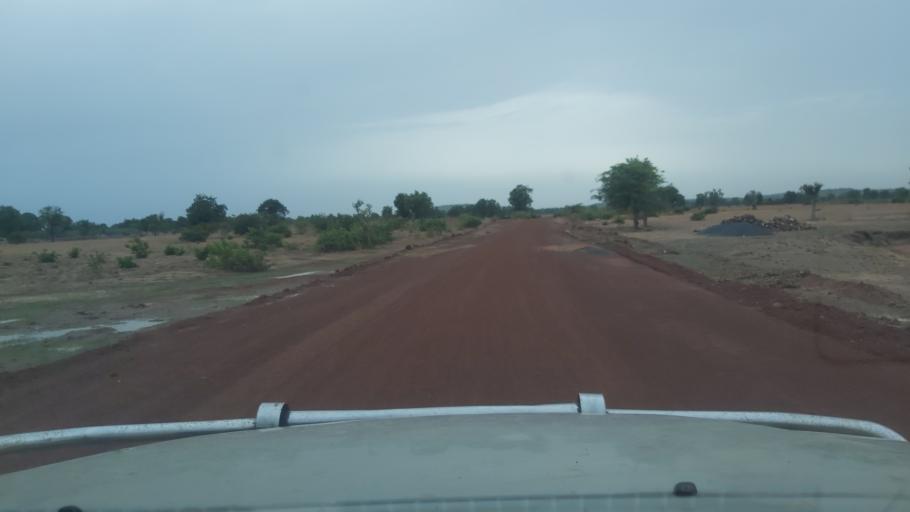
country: ML
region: Koulikoro
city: Banamba
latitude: 13.2743
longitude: -7.5416
